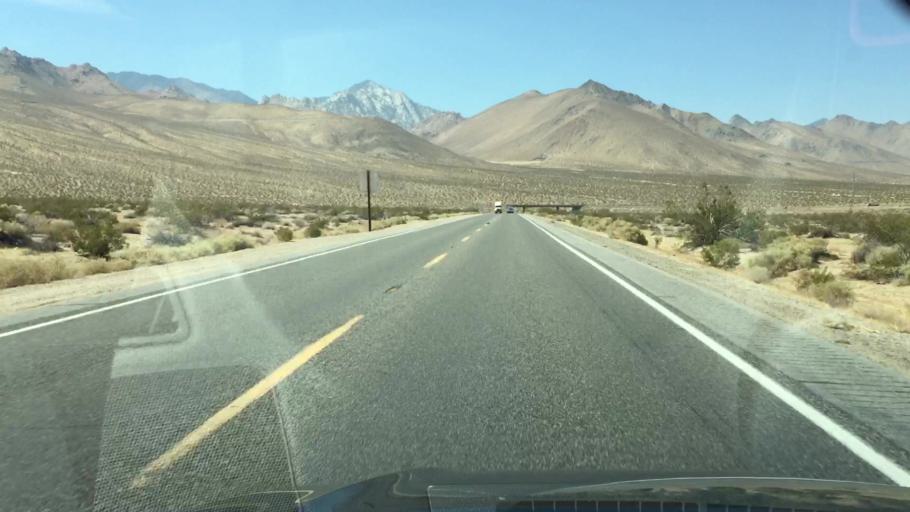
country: US
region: California
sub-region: Kern County
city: Inyokern
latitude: 35.6901
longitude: -117.8593
